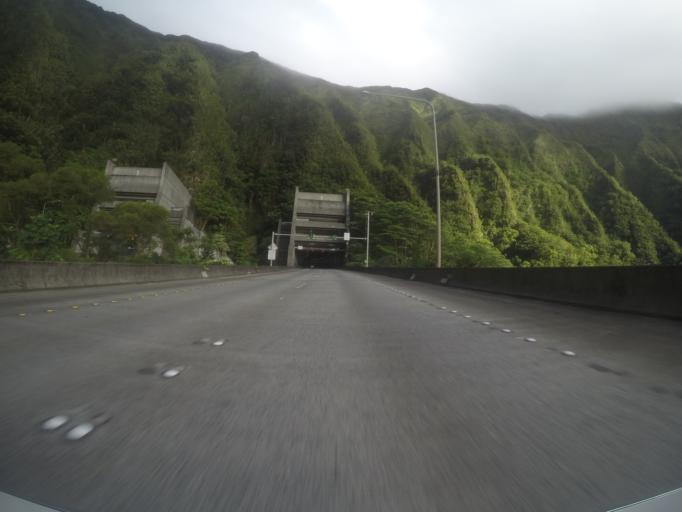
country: US
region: Hawaii
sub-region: Honolulu County
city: Kane'ohe
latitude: 21.4037
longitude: -157.8340
